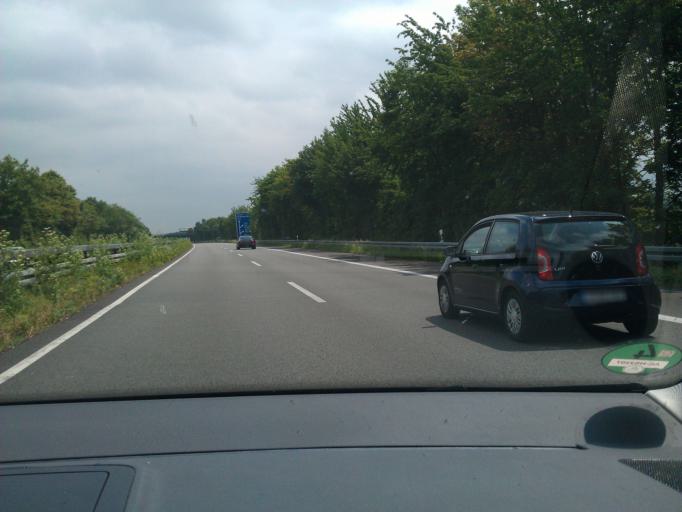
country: DE
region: North Rhine-Westphalia
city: Meckenheim
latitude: 50.6016
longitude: 7.0076
